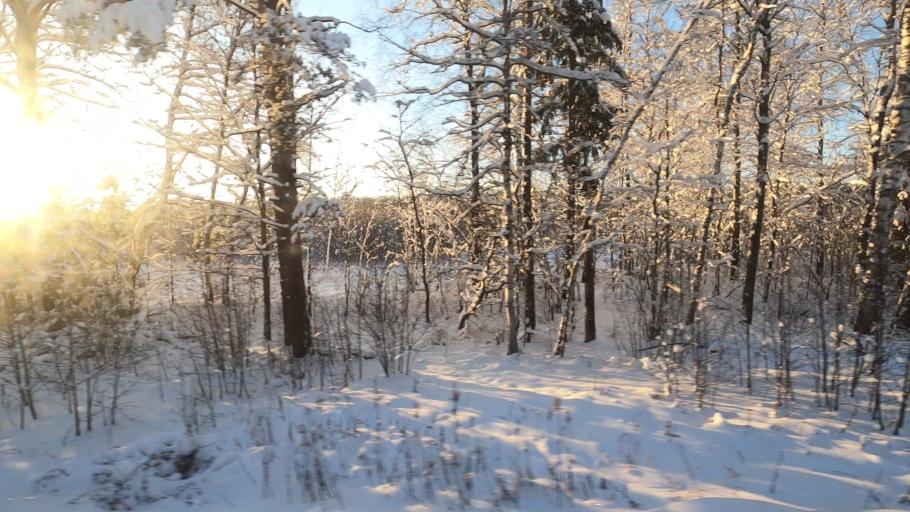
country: RU
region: Moskovskaya
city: Novo-Nikol'skoye
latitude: 56.6357
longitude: 37.5623
